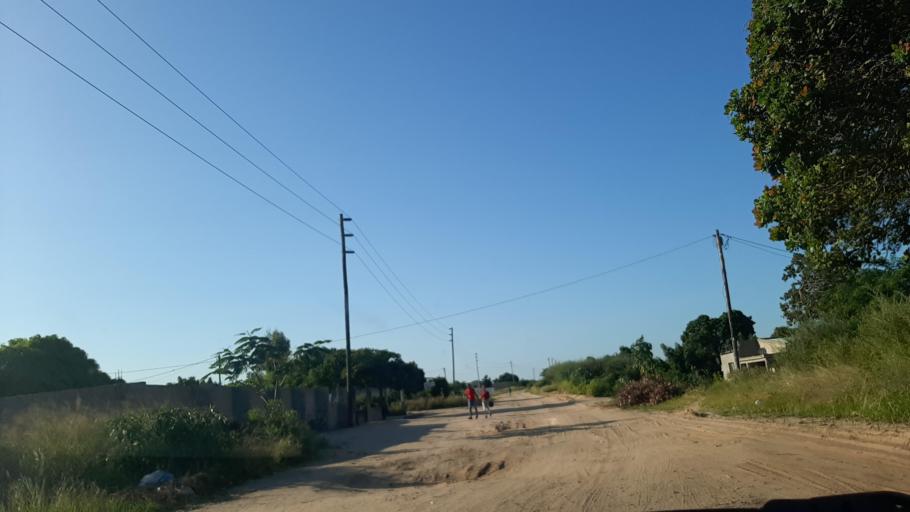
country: MZ
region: Maputo City
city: Maputo
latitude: -25.7568
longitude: 32.5503
